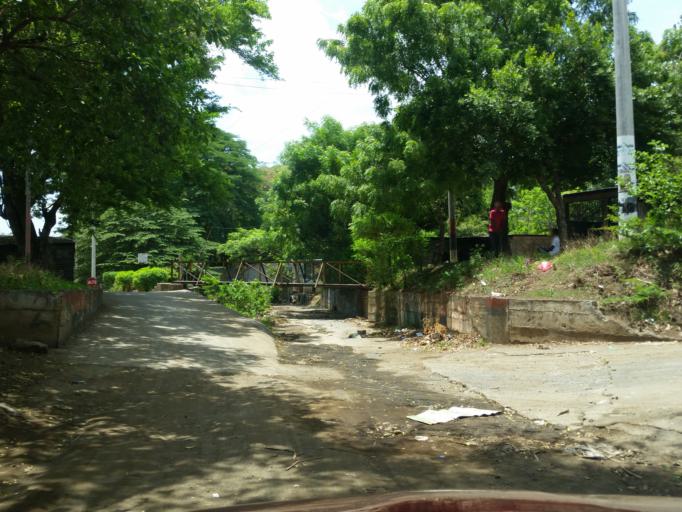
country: NI
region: Managua
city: Managua
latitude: 12.0995
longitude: -86.2750
